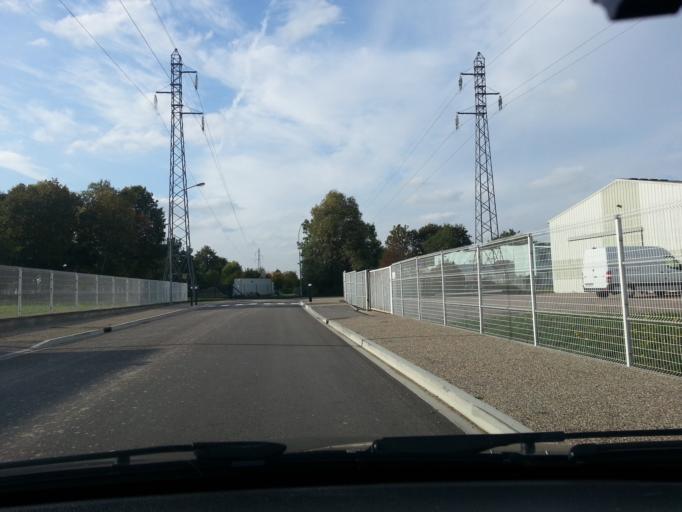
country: FR
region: Bourgogne
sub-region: Departement de Saone-et-Loire
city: Chatenoy-le-Royal
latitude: 46.7974
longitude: 4.7890
